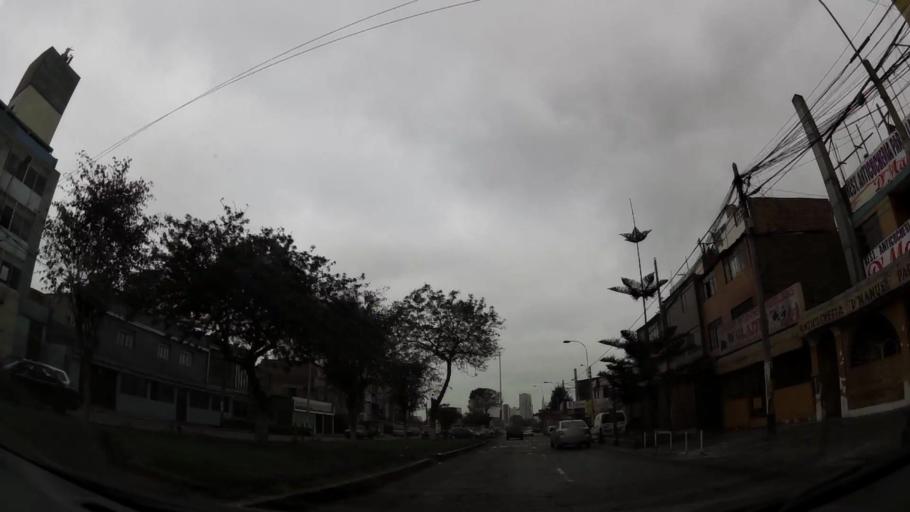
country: PE
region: Lima
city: Lima
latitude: -12.0672
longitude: -77.0594
